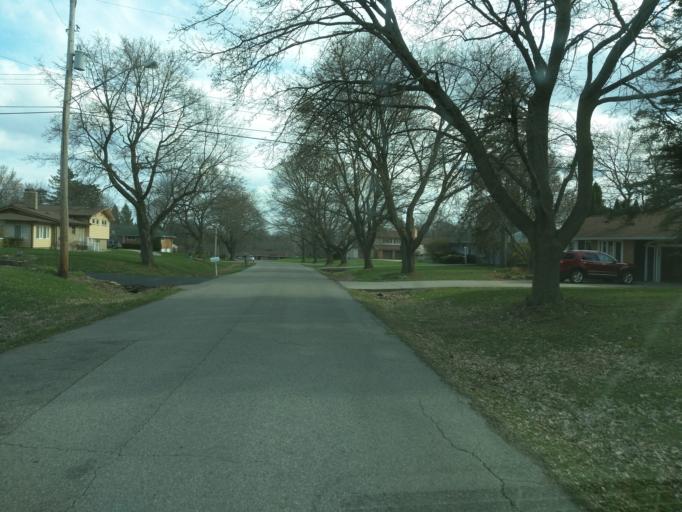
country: US
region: Michigan
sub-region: Ingham County
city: Edgemont Park
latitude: 42.7574
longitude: -84.5985
